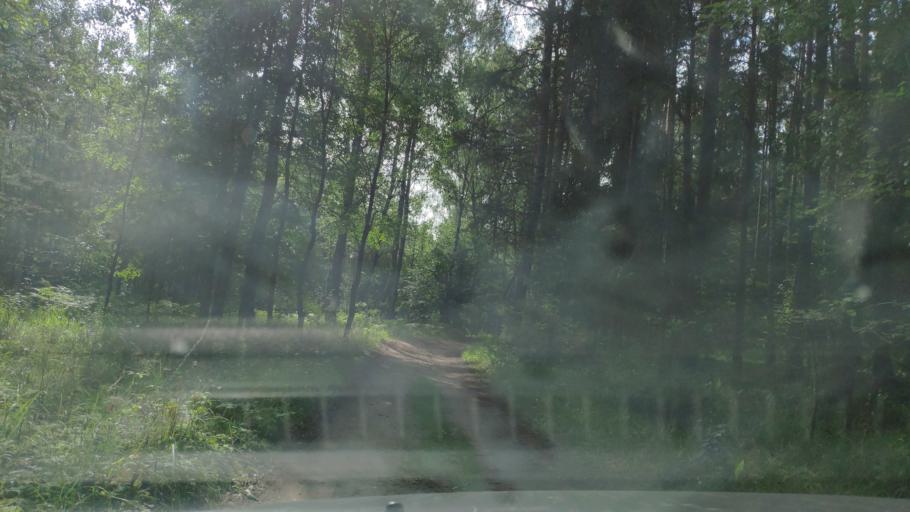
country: BY
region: Minsk
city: Zaslawye
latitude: 53.9703
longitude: 27.2936
